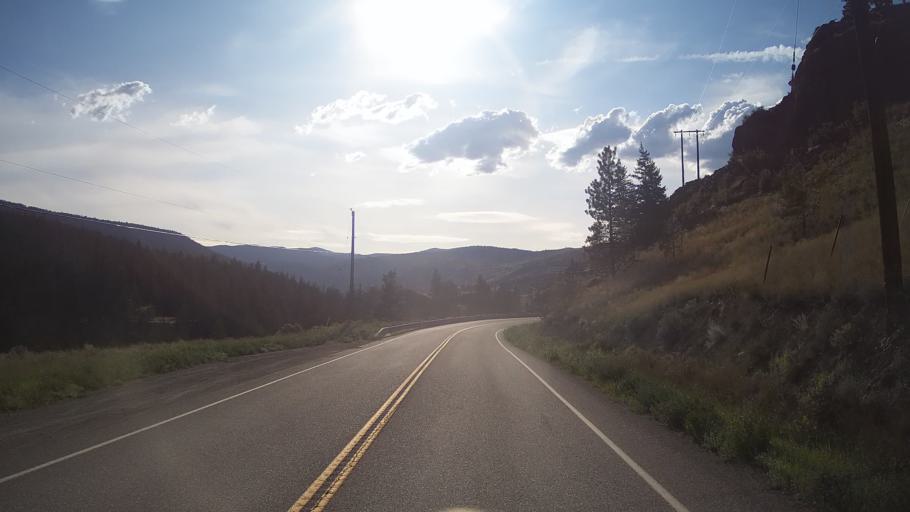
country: CA
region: British Columbia
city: Cache Creek
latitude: 50.8860
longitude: -121.4352
